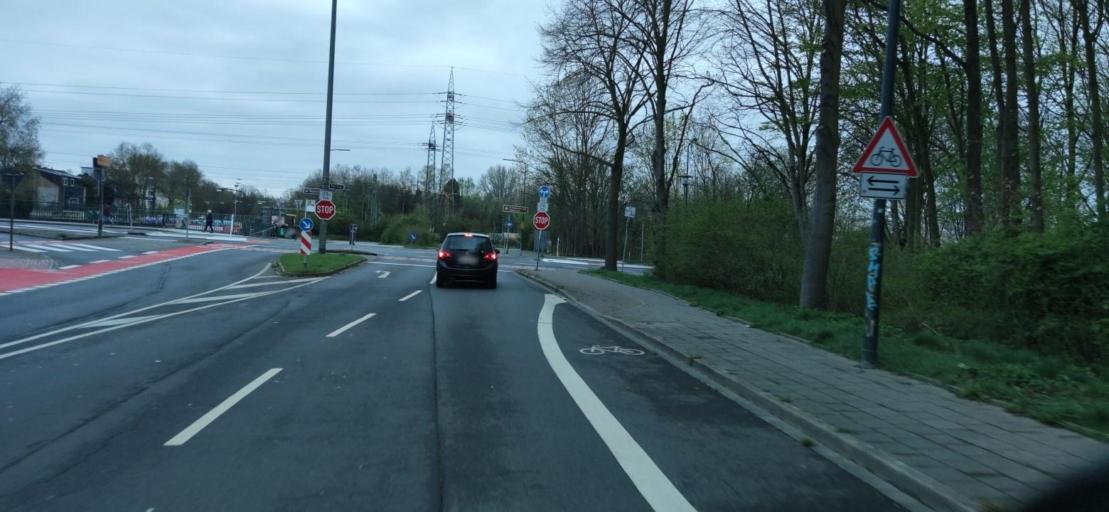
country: DE
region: North Rhine-Westphalia
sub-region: Regierungsbezirk Dusseldorf
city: Erkrath
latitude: 51.2042
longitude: 6.8523
